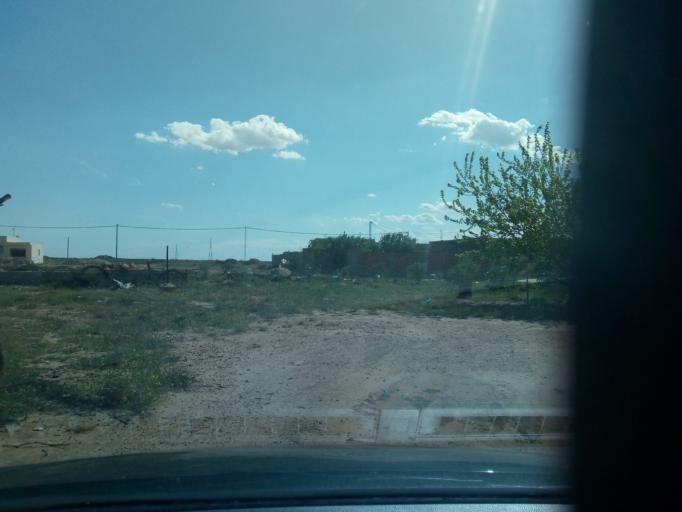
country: TN
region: Safaqis
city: Sfax
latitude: 34.7257
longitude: 10.6041
